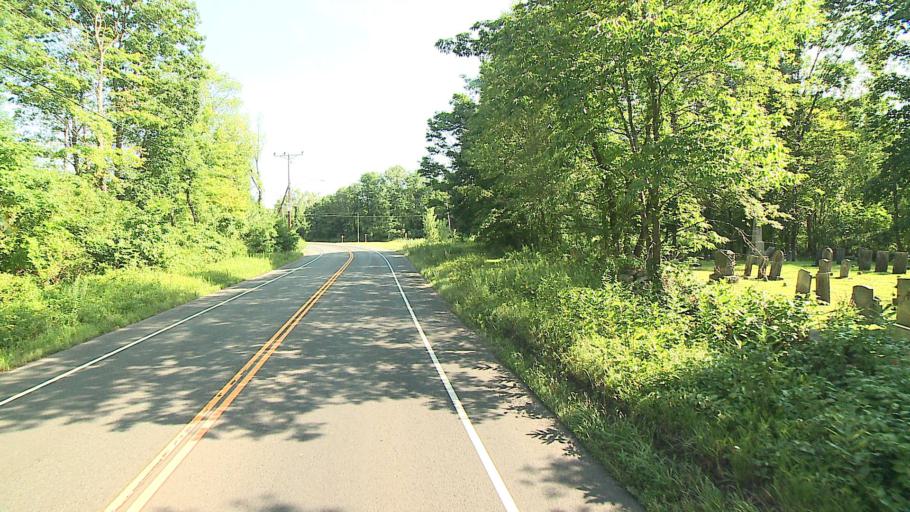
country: US
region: Connecticut
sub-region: Fairfield County
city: Georgetown
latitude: 41.2911
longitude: -73.4509
